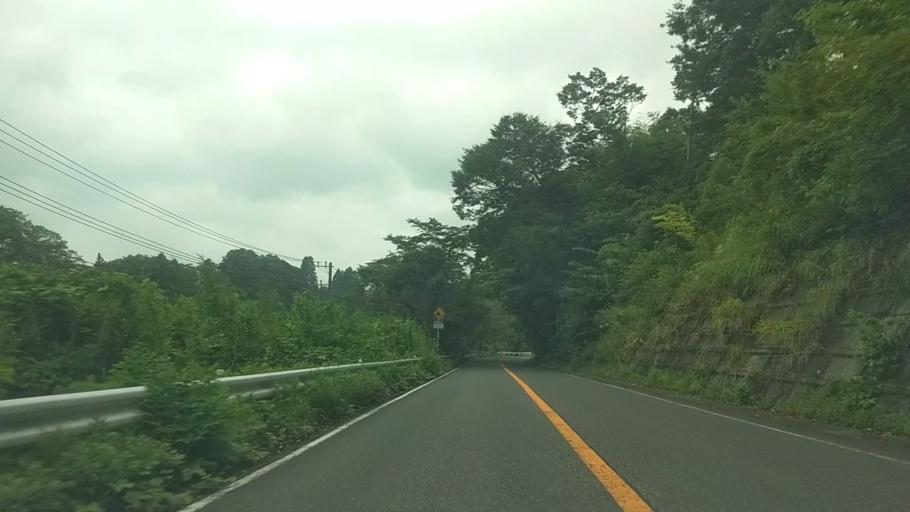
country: JP
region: Chiba
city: Kawaguchi
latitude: 35.2408
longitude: 140.0722
